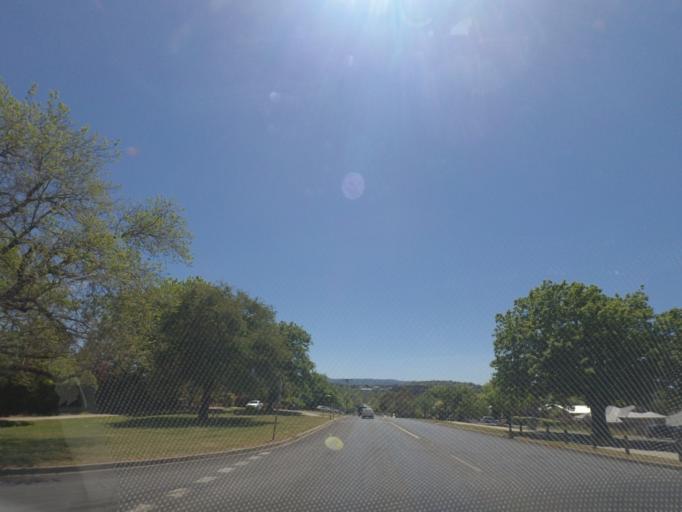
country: AU
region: Victoria
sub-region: Hume
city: Sunbury
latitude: -37.4921
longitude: 144.5904
